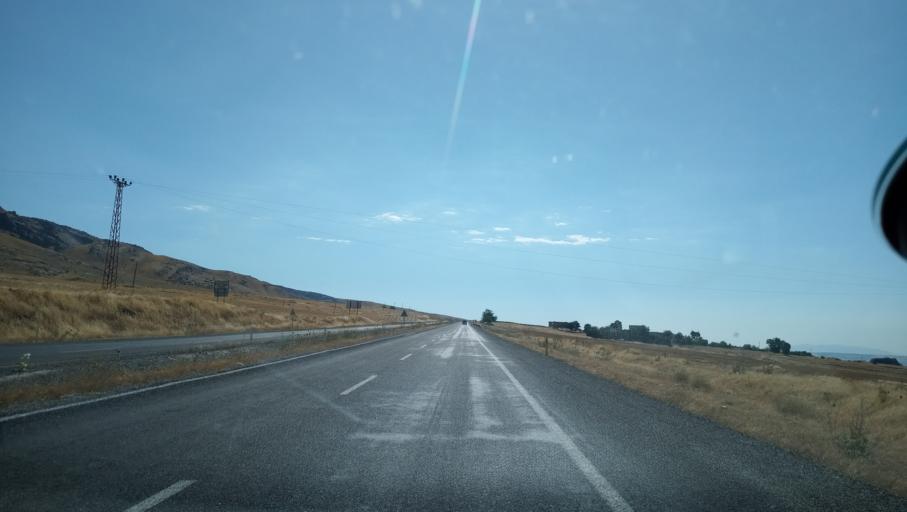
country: TR
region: Diyarbakir
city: Silvan
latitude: 38.1280
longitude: 41.0586
